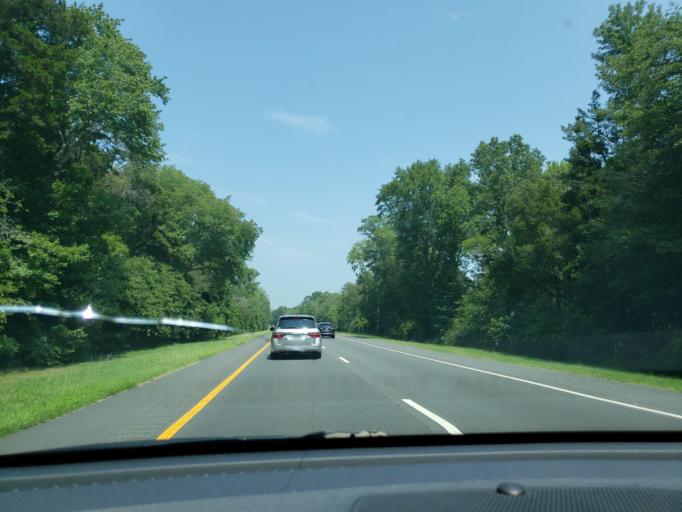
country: US
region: New Jersey
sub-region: Cape May County
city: Avalon
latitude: 39.1349
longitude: -74.7656
